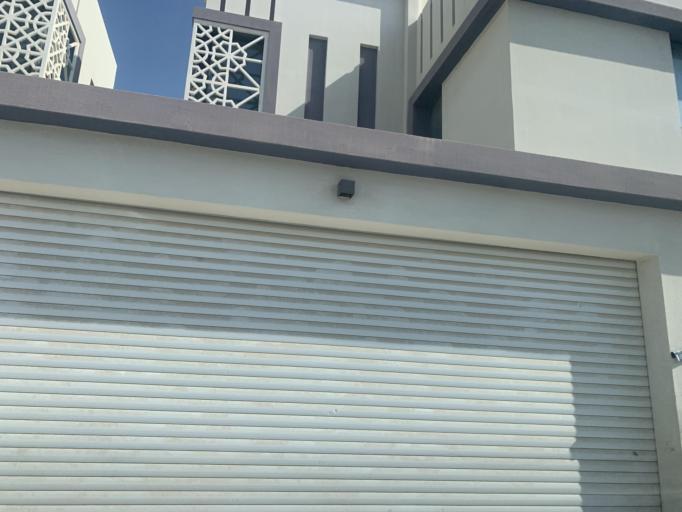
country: BH
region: Central Governorate
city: Madinat Hamad
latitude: 26.1323
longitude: 50.4833
